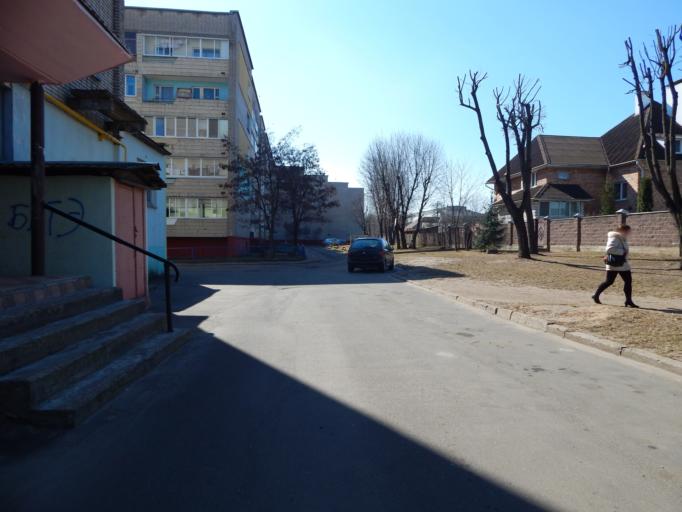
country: BY
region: Minsk
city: Horad Barysaw
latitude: 54.2123
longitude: 28.5031
